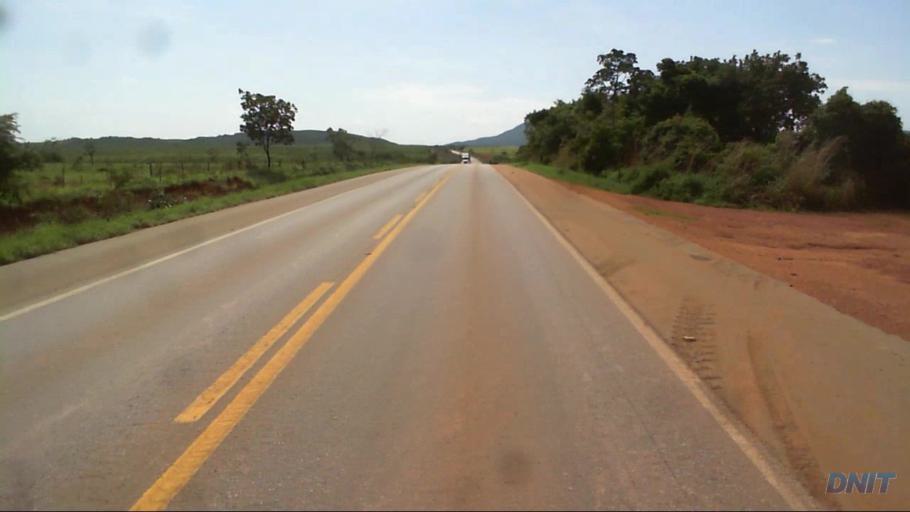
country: BR
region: Goias
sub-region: Barro Alto
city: Barro Alto
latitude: -15.1876
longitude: -48.7789
